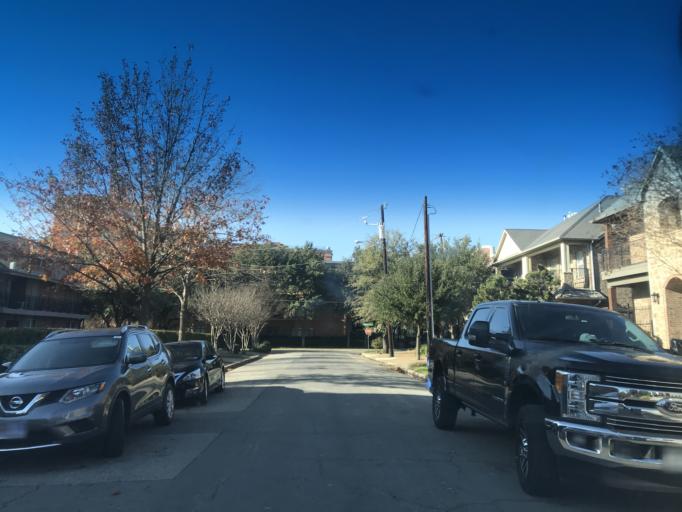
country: US
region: Texas
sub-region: Dallas County
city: Highland Park
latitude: 32.8215
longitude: -96.8113
